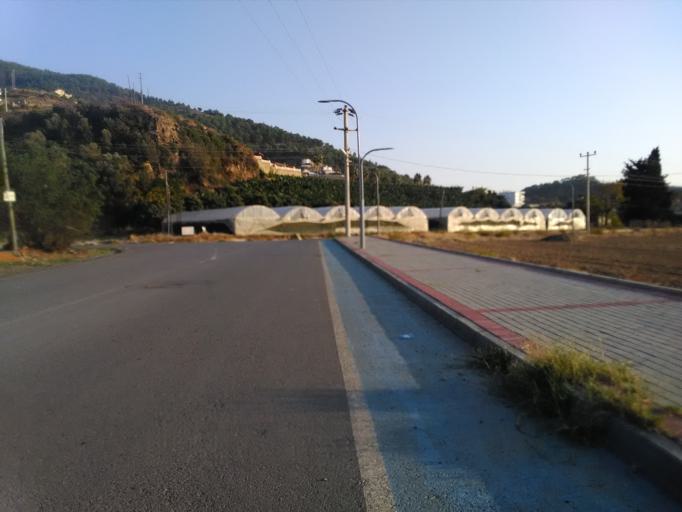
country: TR
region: Antalya
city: Gazipasa
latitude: 36.2412
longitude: 32.2994
